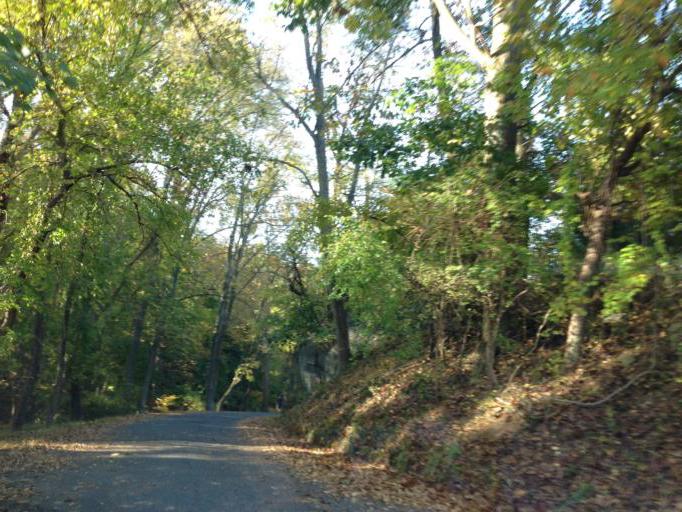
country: US
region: Maryland
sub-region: Howard County
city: Ellicott City
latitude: 39.2803
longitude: -76.7916
